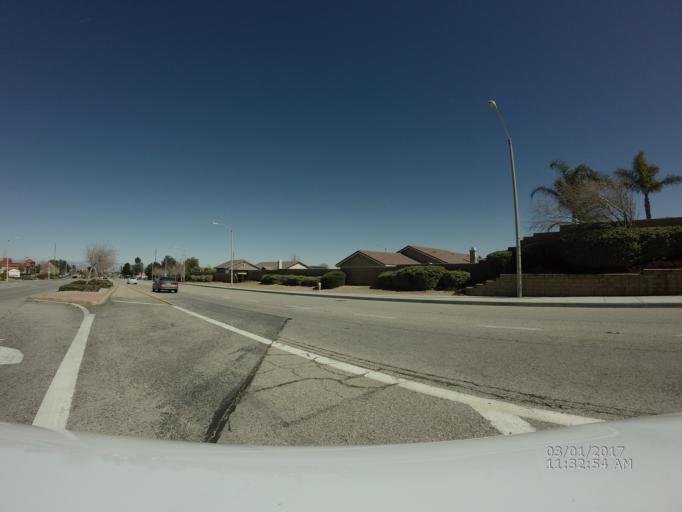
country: US
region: California
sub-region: Los Angeles County
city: Quartz Hill
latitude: 34.6289
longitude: -118.2188
